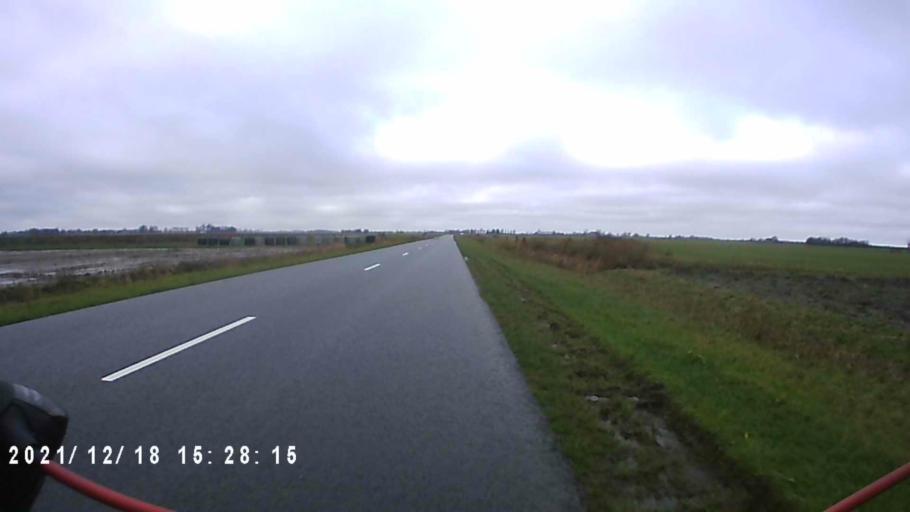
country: NL
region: Friesland
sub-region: Gemeente Dongeradeel
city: Anjum
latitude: 53.3316
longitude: 6.1447
